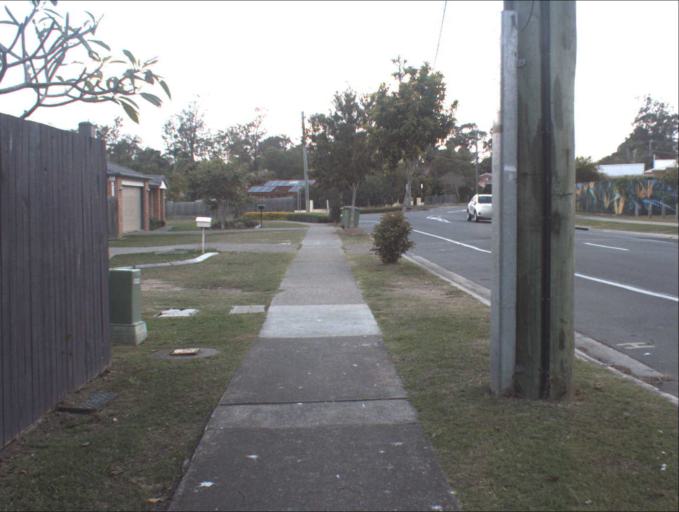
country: AU
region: Queensland
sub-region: Logan
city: Waterford West
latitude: -27.6770
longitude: 153.1316
